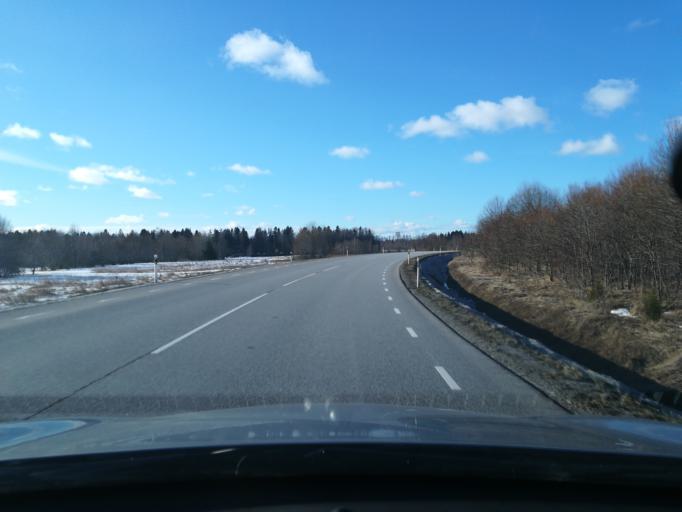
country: EE
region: Harju
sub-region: Saku vald
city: Saku
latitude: 59.2734
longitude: 24.6901
